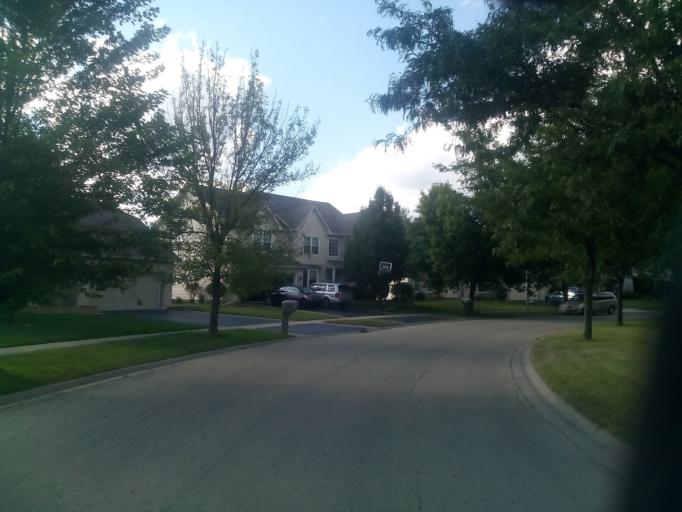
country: US
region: Illinois
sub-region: Will County
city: Plainfield
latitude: 41.6931
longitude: -88.1582
